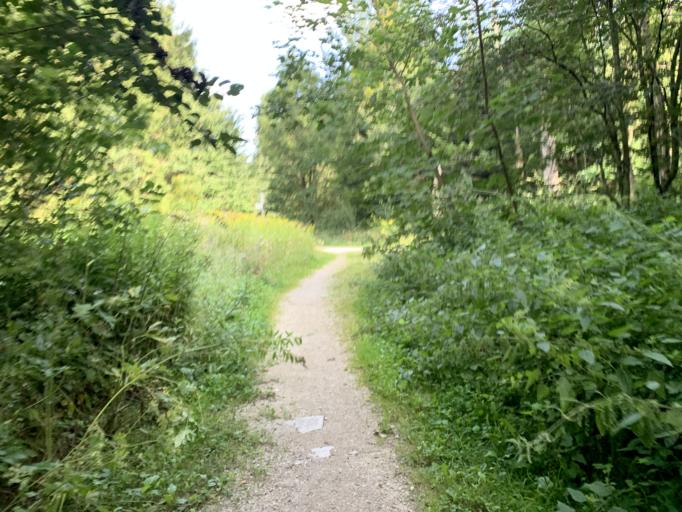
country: DE
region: Bavaria
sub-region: Upper Bavaria
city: Freising
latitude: 48.4201
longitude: 11.7406
